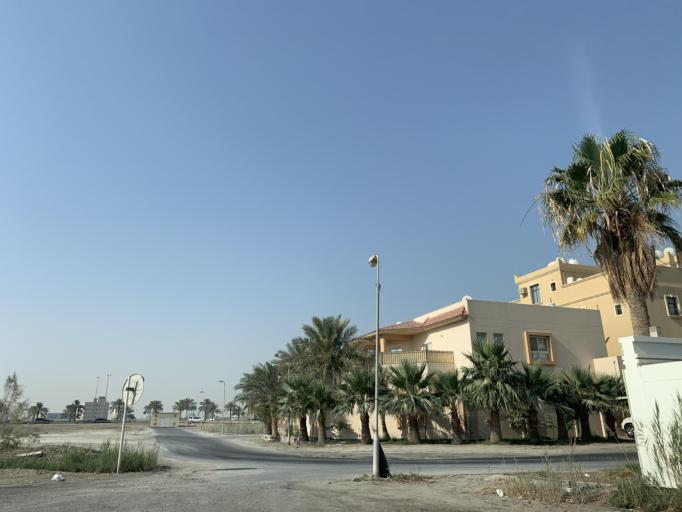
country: BH
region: Northern
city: Madinat `Isa
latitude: 26.1945
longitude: 50.5169
